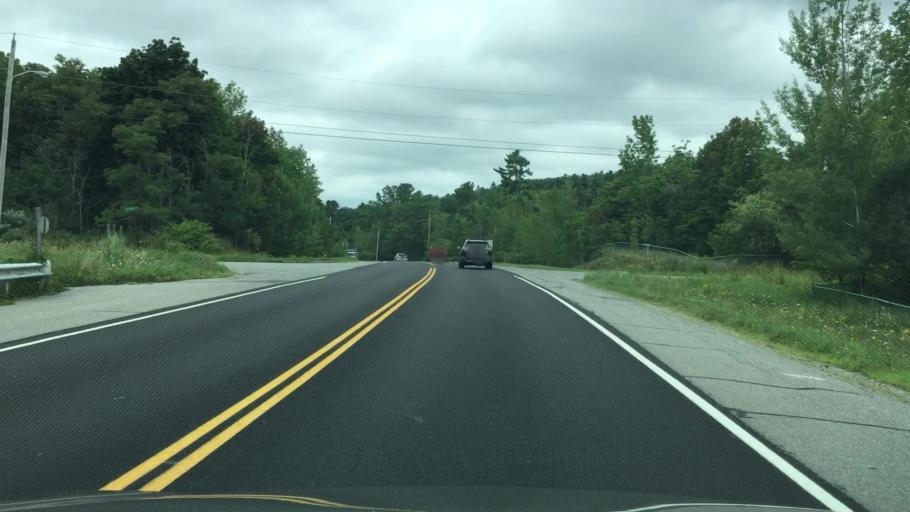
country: US
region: Maine
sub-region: Penobscot County
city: Orrington
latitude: 44.6896
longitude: -68.8107
